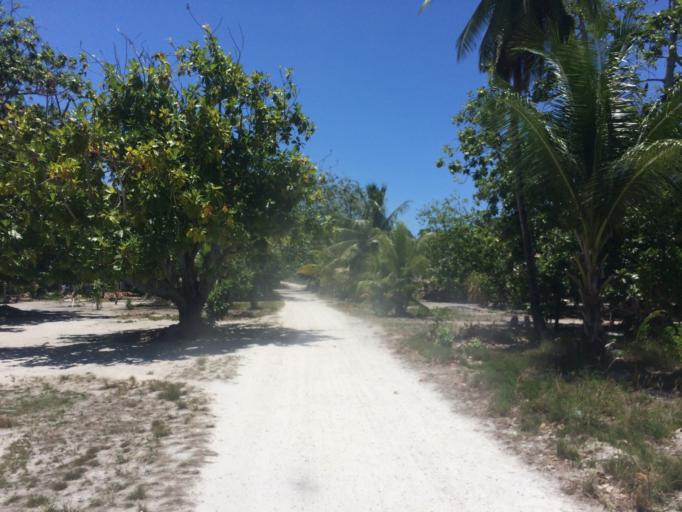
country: KI
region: Gilbert Islands
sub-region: Marakei
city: Rawannawi Village
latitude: 1.7547
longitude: 173.0417
